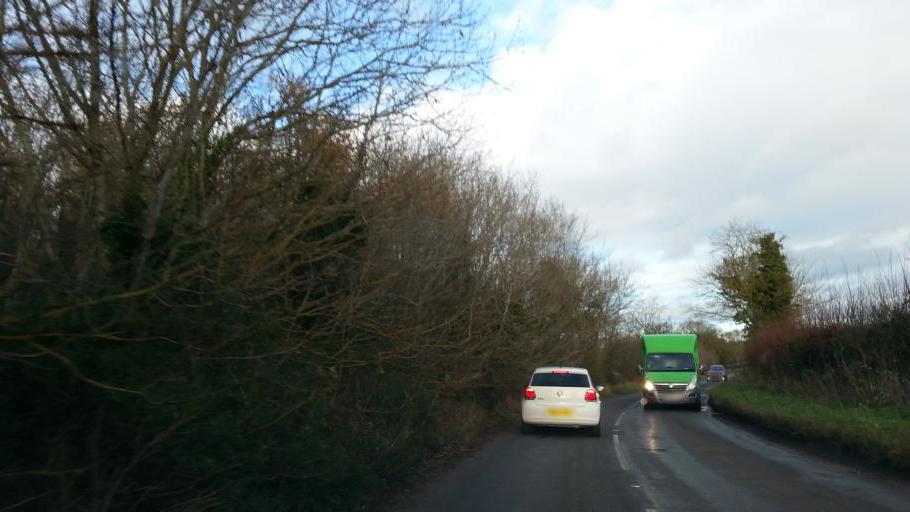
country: GB
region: England
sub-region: Oxfordshire
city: Stanford in the Vale
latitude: 51.6641
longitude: -1.4906
